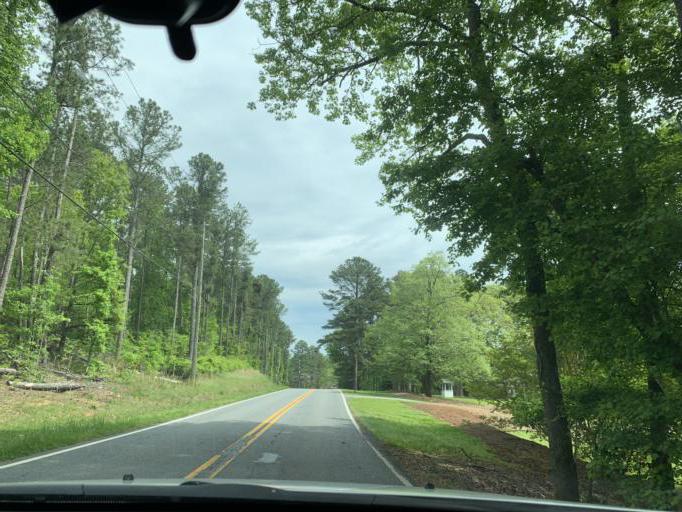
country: US
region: Georgia
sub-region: Forsyth County
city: Cumming
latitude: 34.1336
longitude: -84.1899
